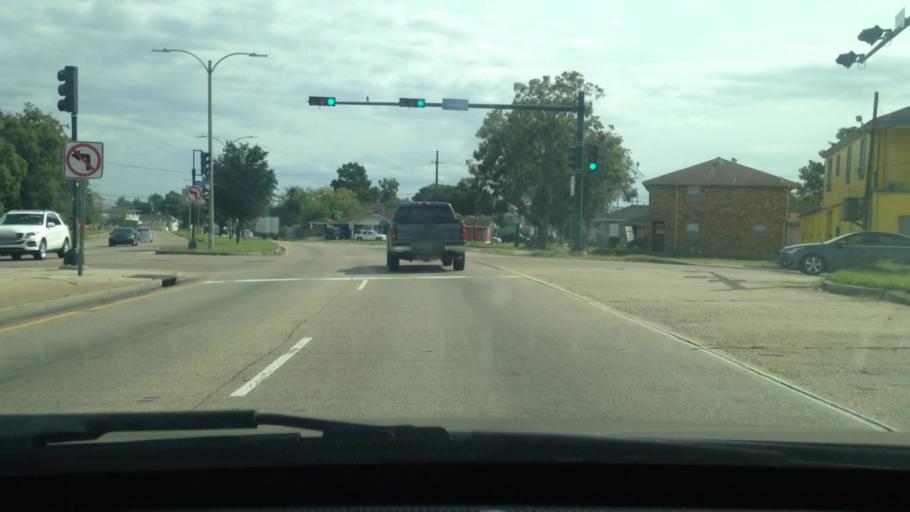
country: US
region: Louisiana
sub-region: Jefferson Parish
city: Jefferson
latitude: 29.9656
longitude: -90.1260
